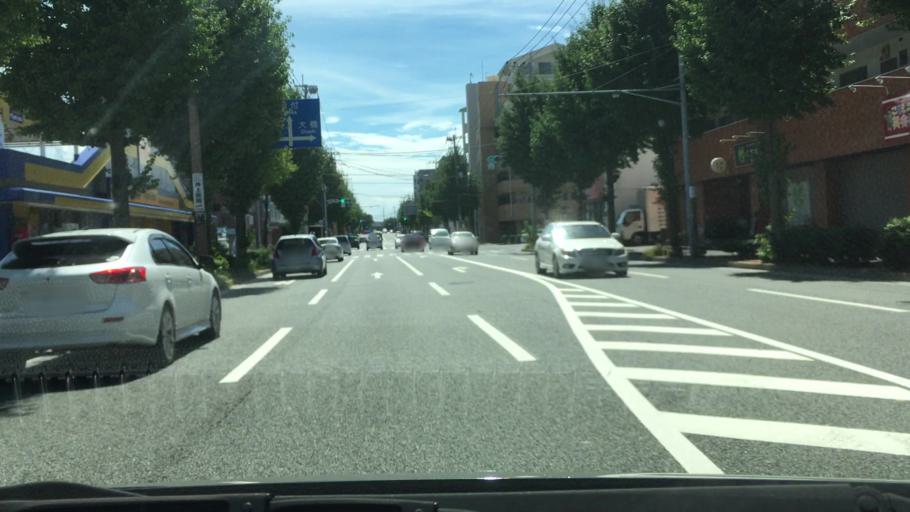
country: JP
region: Fukuoka
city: Fukuoka-shi
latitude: 33.5646
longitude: 130.4297
